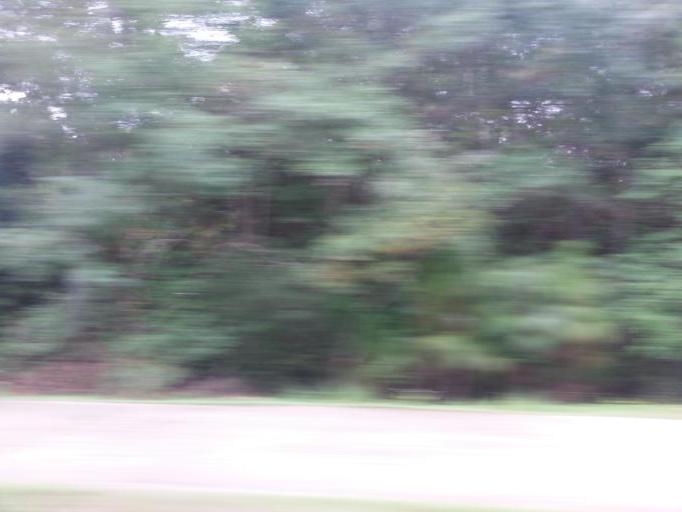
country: US
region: Alabama
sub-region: Baldwin County
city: Point Clear
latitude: 30.4334
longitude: -87.9110
